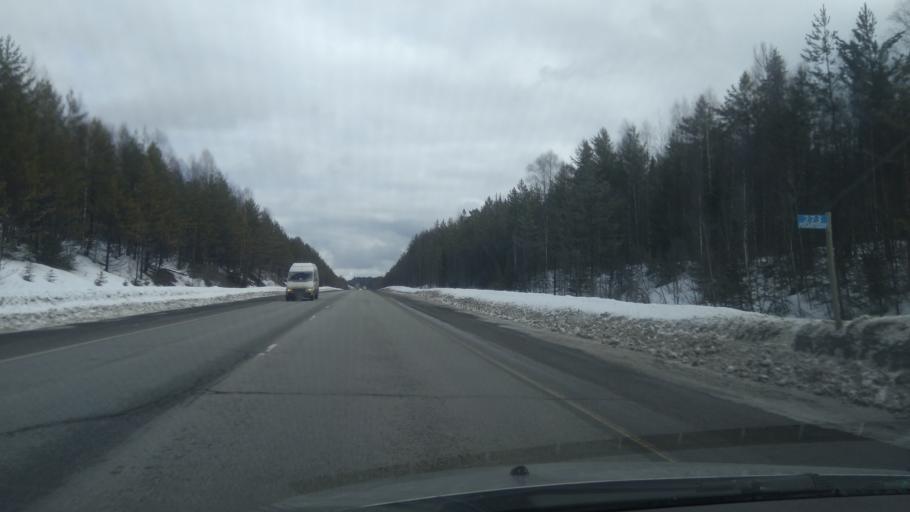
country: RU
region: Sverdlovsk
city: Nizhniye Sergi
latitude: 56.8247
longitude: 59.2760
